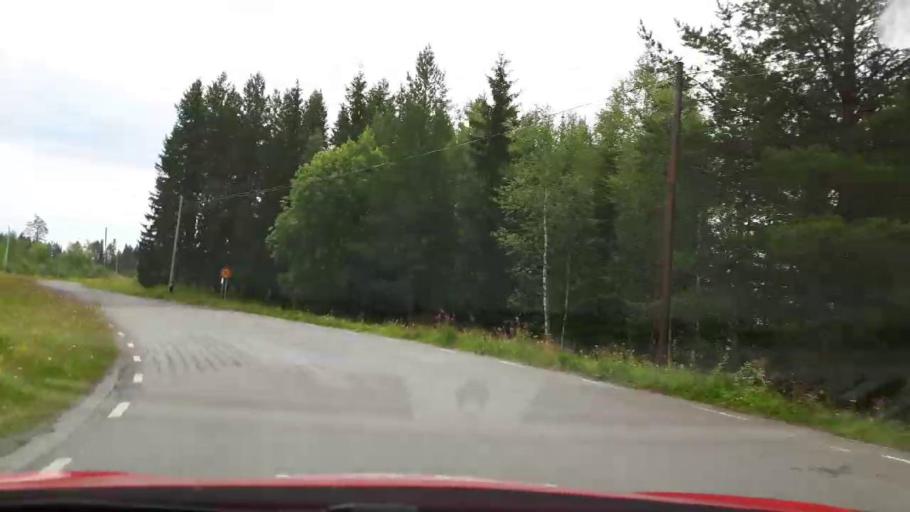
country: SE
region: Jaemtland
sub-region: OEstersunds Kommun
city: Lit
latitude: 63.3943
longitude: 15.0090
